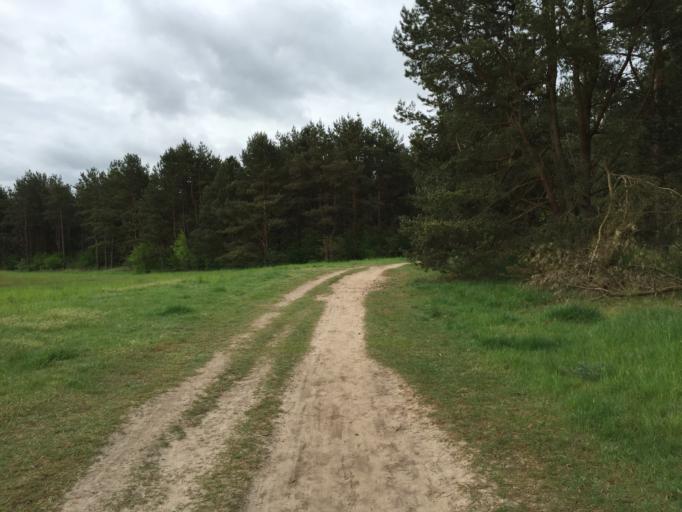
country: SE
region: Skane
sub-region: Lunds Kommun
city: Veberod
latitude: 55.6262
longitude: 13.4955
